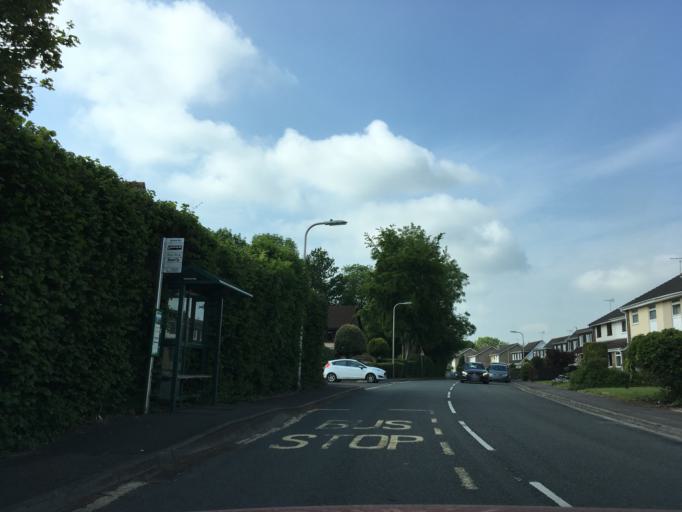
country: GB
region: England
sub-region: North Somerset
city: Nailsea
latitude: 51.4292
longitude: -2.7462
